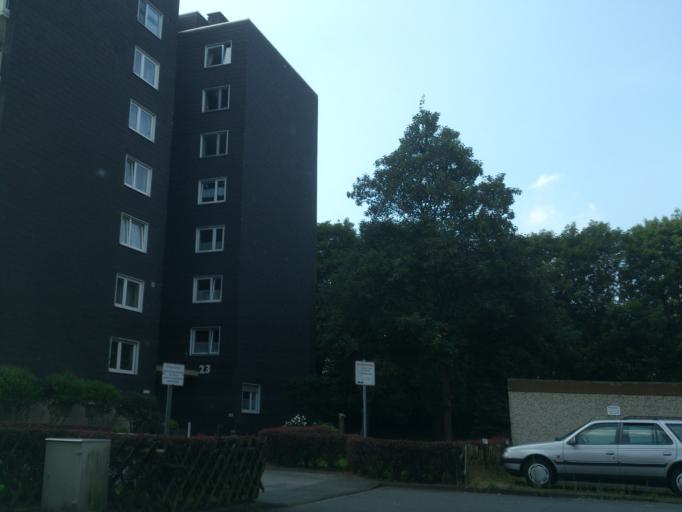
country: DE
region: North Rhine-Westphalia
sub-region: Regierungsbezirk Detmold
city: Paderborn
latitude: 51.7163
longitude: 8.7226
